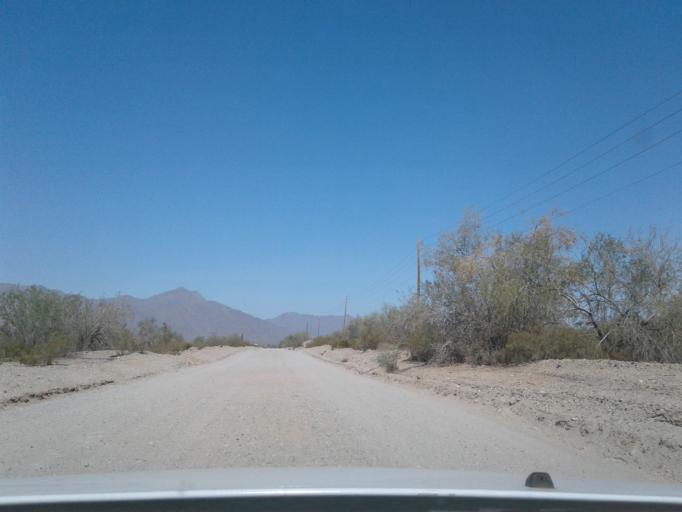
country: US
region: Arizona
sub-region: Maricopa County
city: Laveen
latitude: 33.2905
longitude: -112.1437
